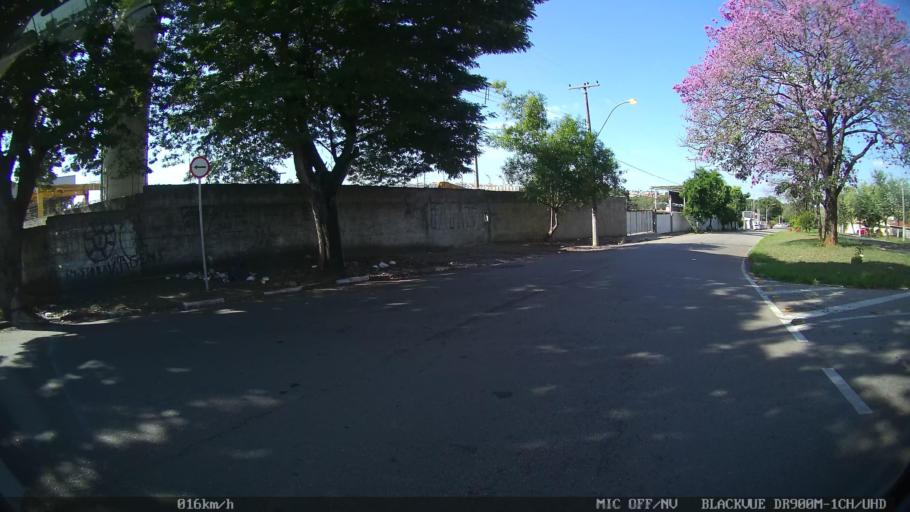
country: BR
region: Sao Paulo
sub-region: Sumare
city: Sumare
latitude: -22.8087
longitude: -47.2811
